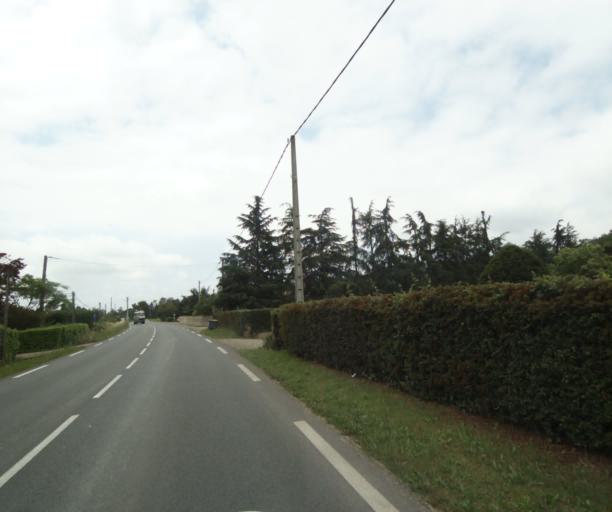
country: FR
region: Midi-Pyrenees
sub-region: Departement du Tarn-et-Garonne
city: Montauban
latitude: 43.9948
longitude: 1.3856
